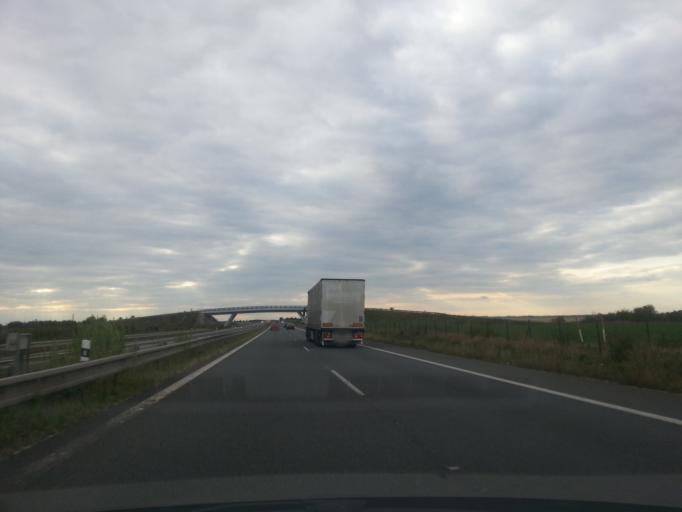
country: CZ
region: Central Bohemia
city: Hostivice
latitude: 50.0949
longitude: 14.2383
